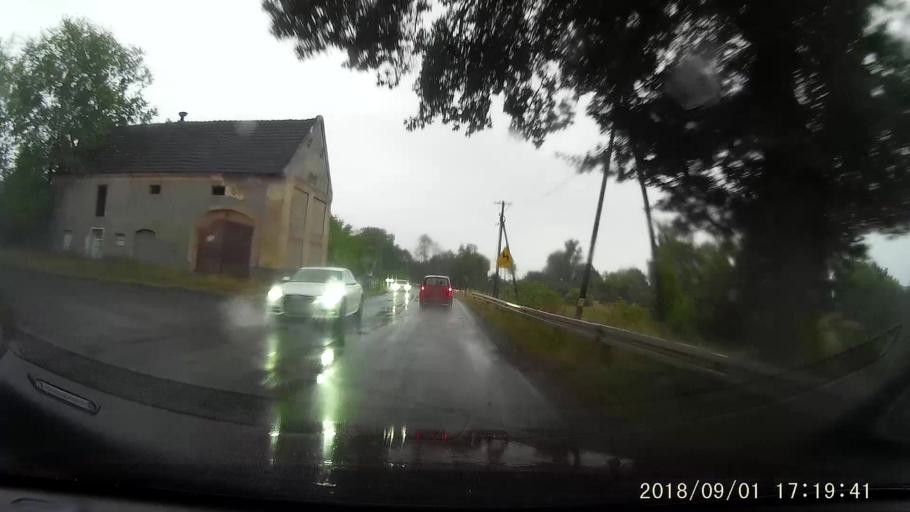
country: PL
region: Lubusz
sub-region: Powiat zielonogorski
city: Nowogrod Bobrzanski
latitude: 51.7300
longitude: 15.2739
